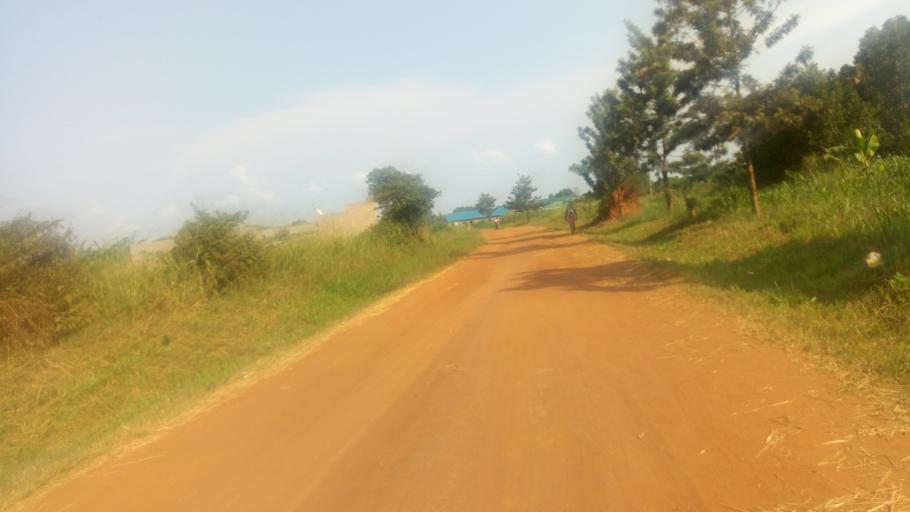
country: UG
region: Western Region
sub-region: Kiryandongo District
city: Kiryandongo
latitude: 1.8068
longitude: 32.0077
